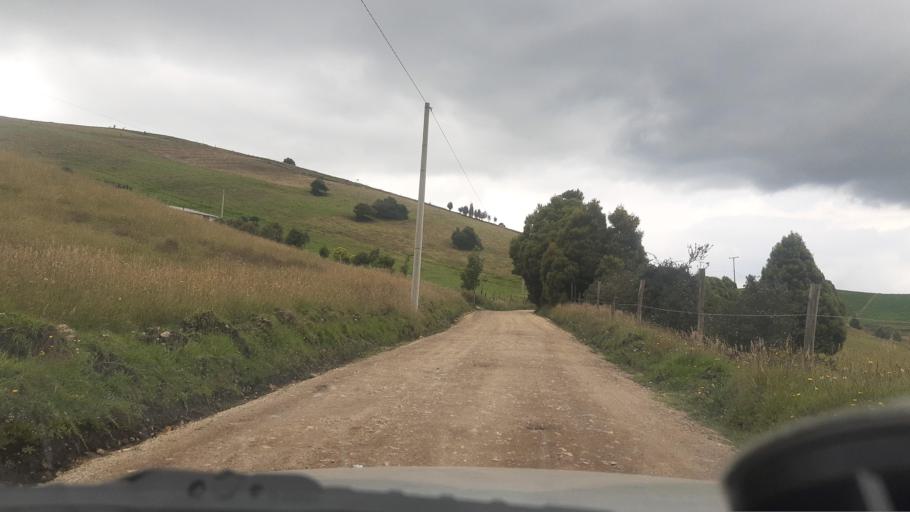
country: CO
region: Cundinamarca
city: Suesca
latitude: 5.1394
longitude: -73.7917
